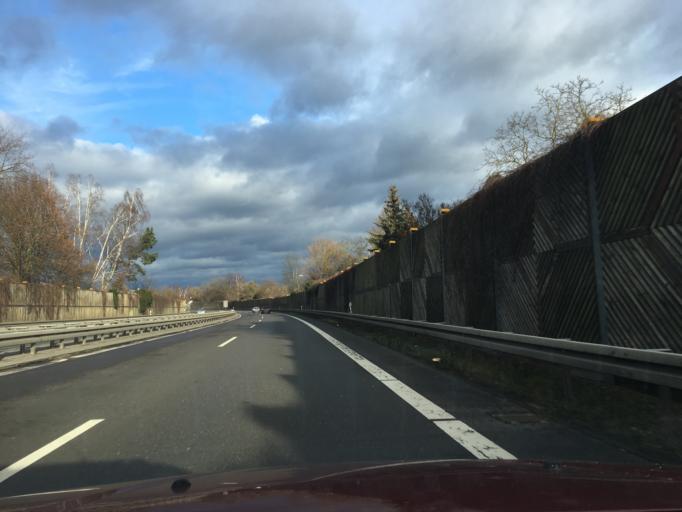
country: DE
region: Berlin
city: Bohnsdorf
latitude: 52.3897
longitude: 13.5647
